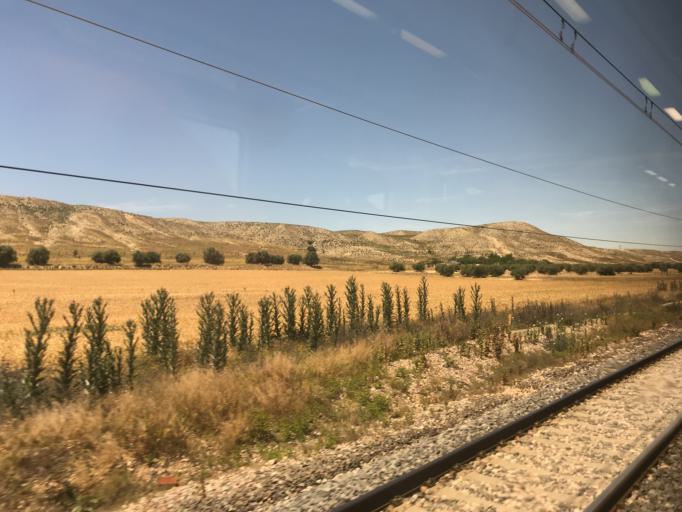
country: ES
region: Madrid
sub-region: Provincia de Madrid
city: Ciempozuelos
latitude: 40.1266
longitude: -3.6166
